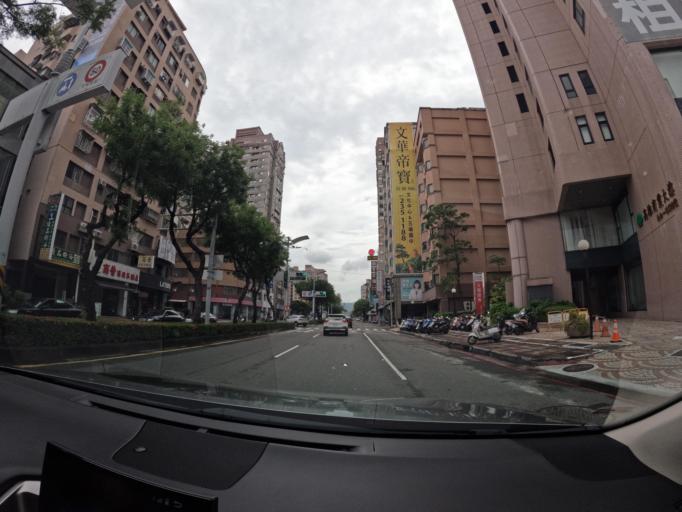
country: TW
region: Kaohsiung
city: Kaohsiung
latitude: 22.6393
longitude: 120.3275
